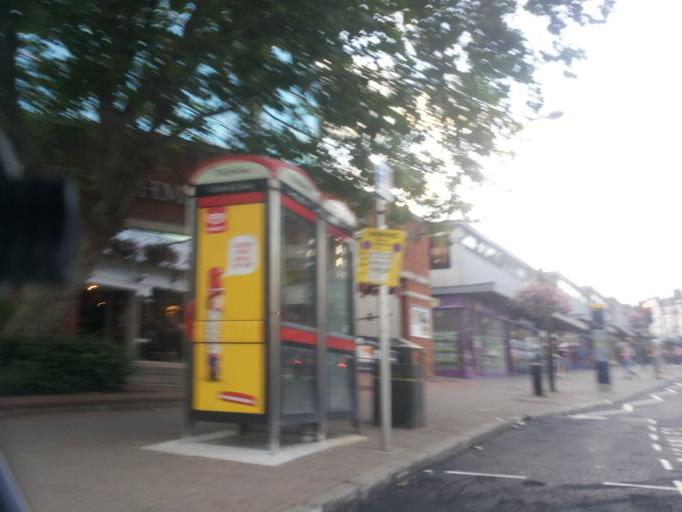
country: GB
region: England
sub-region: Greater London
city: Bromley
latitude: 51.3995
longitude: 0.0169
